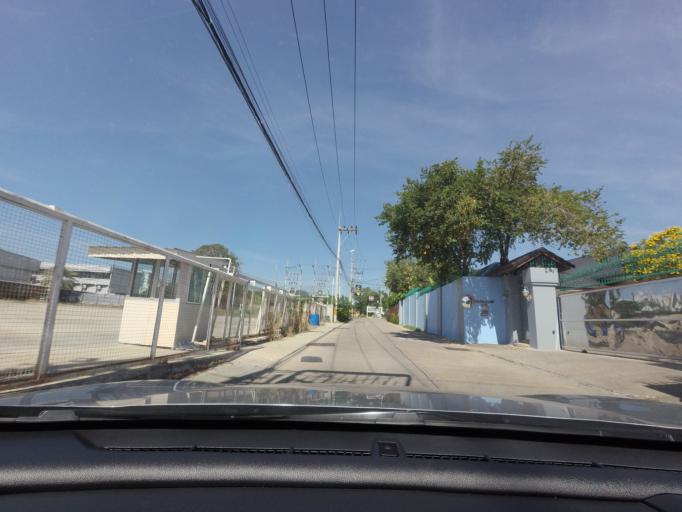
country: TH
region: Chon Buri
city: Phatthaya
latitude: 12.9455
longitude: 100.8982
